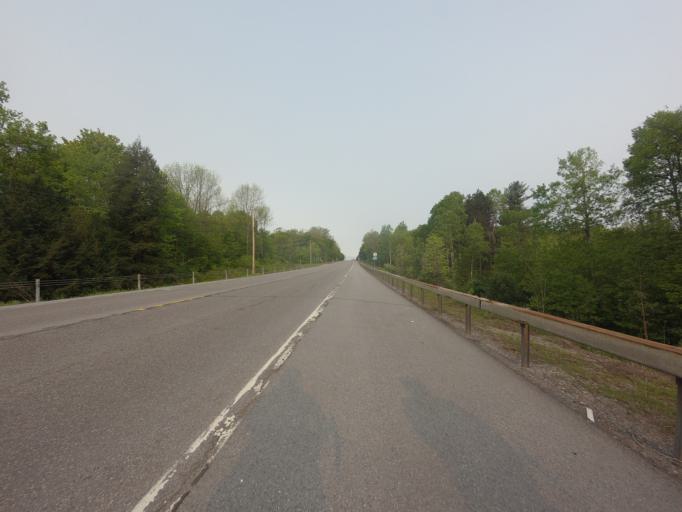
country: US
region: New York
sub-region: Jefferson County
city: Carthage
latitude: 44.0740
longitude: -75.4618
